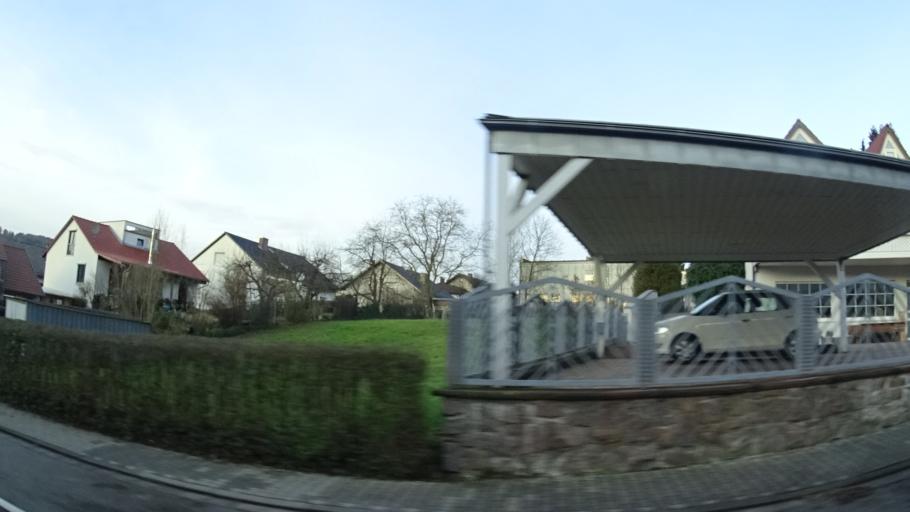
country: DE
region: Hesse
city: Reichelsheim
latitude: 49.7066
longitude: 8.8326
